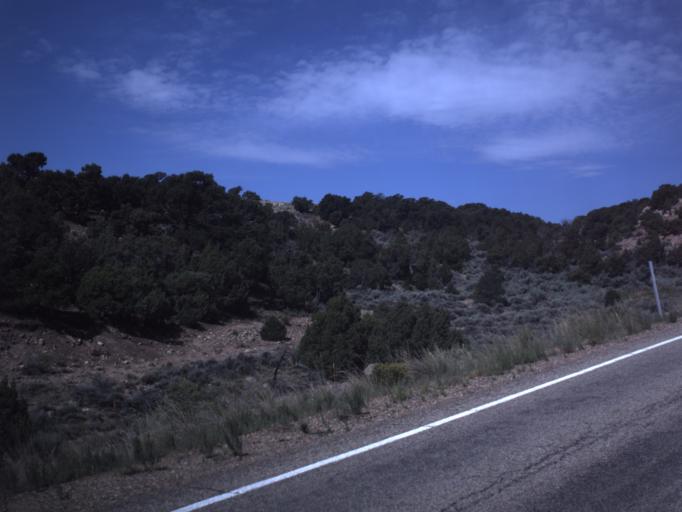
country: US
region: Utah
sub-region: Duchesne County
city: Duchesne
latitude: 40.3136
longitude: -110.3813
